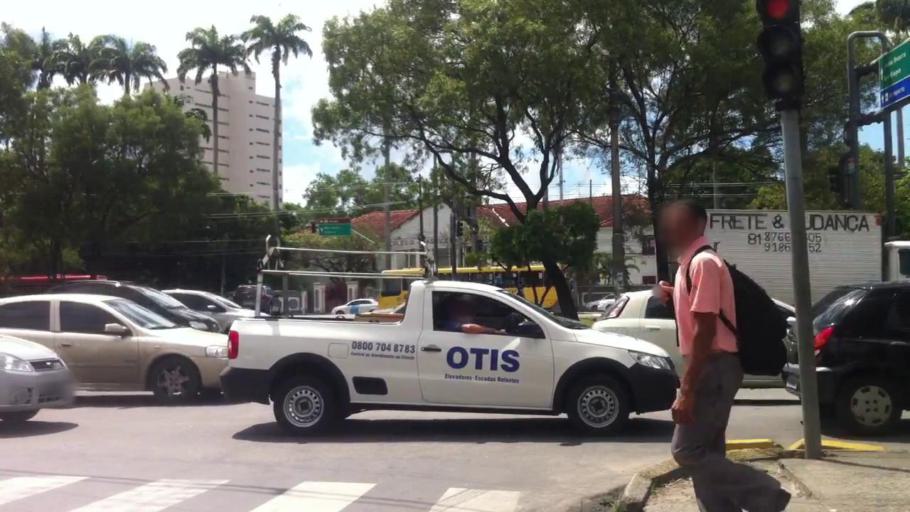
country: BR
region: Pernambuco
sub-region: Recife
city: Recife
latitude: -8.0523
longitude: -34.8953
